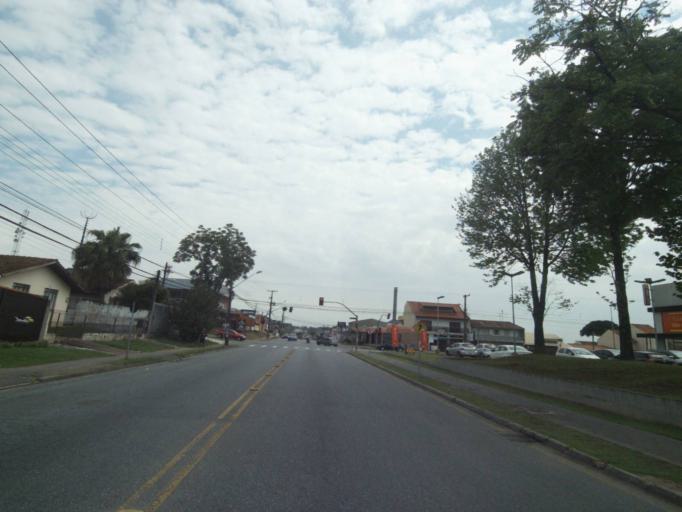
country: BR
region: Parana
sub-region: Pinhais
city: Pinhais
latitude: -25.3967
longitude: -49.2086
